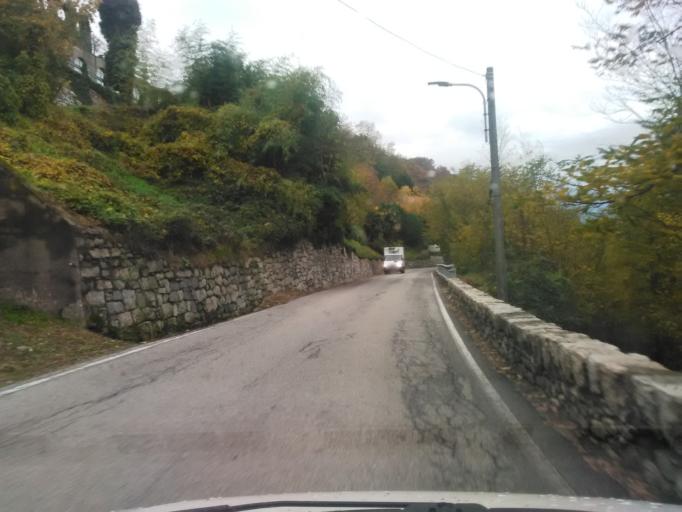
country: IT
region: Piedmont
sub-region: Provincia di Novara
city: Pogno
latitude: 45.7594
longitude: 8.3857
